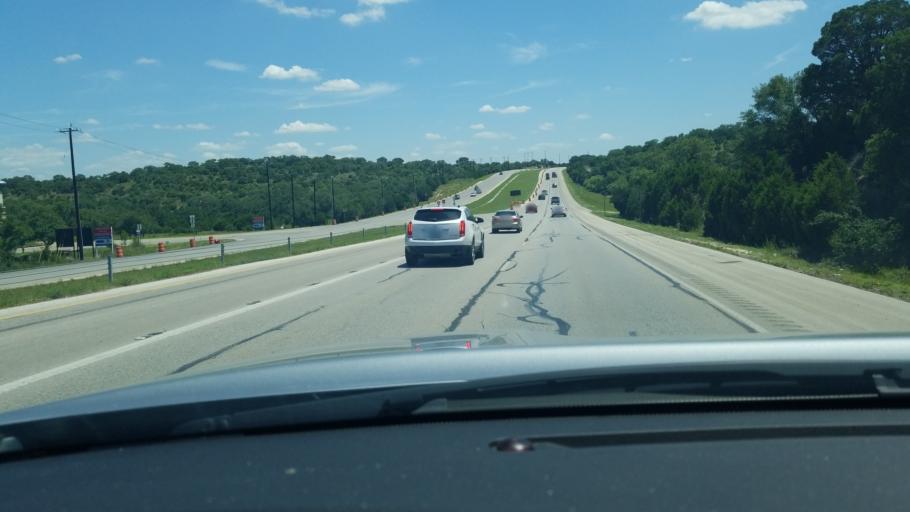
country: US
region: Texas
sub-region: Comal County
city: Bulverde
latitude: 29.7718
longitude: -98.4276
